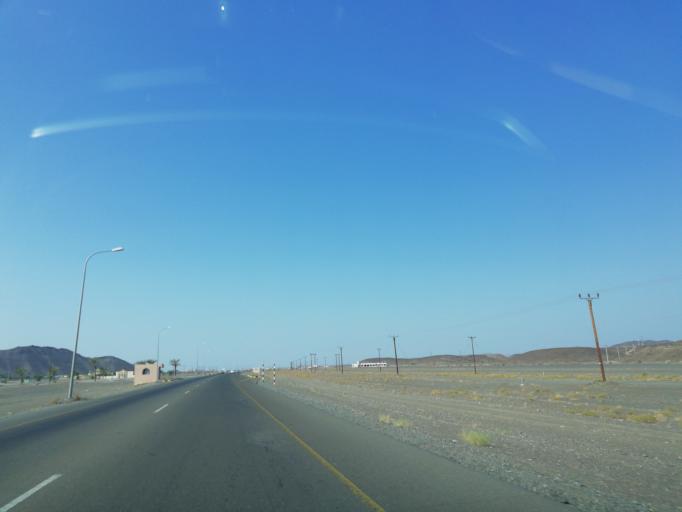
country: OM
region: Ash Sharqiyah
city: Ibra'
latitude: 22.7232
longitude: 58.1491
